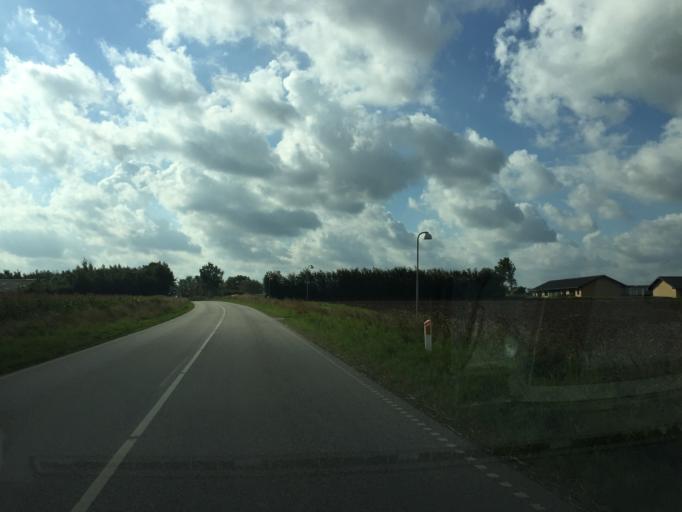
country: DK
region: South Denmark
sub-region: Sonderborg Kommune
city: Grasten
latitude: 55.0022
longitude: 9.5797
